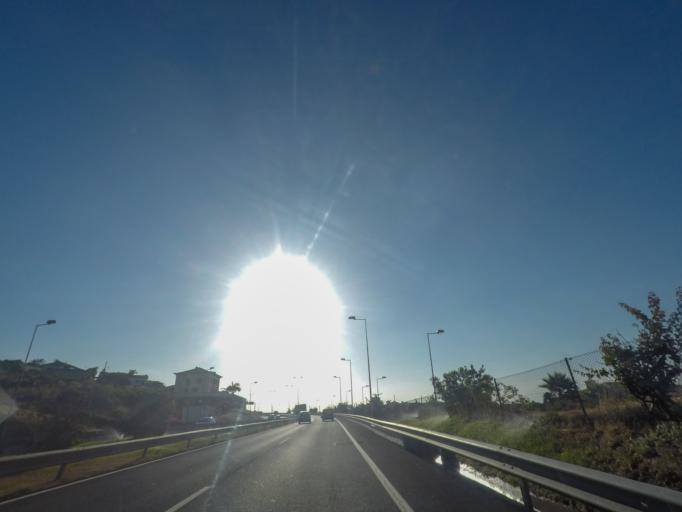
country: PT
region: Madeira
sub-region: Santa Cruz
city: Santa Cruz
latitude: 32.6547
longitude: -16.8178
